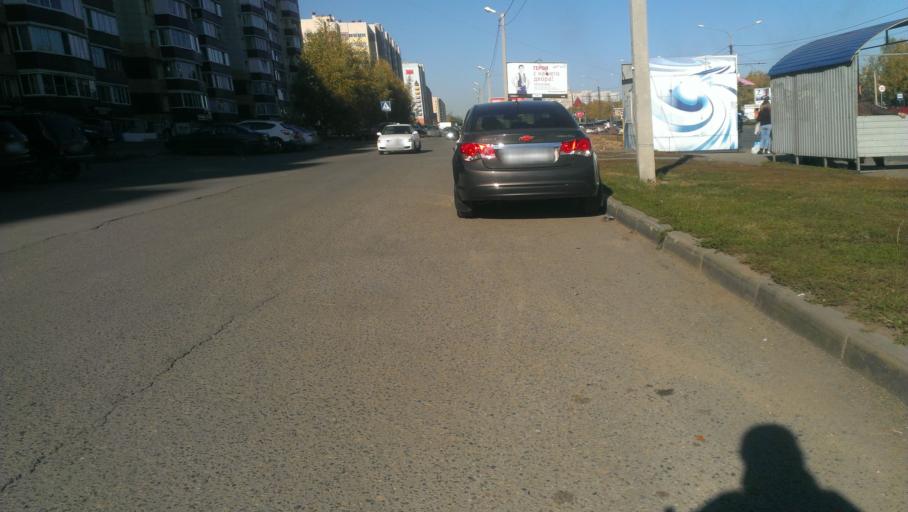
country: RU
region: Altai Krai
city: Novosilikatnyy
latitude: 53.3300
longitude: 83.6921
